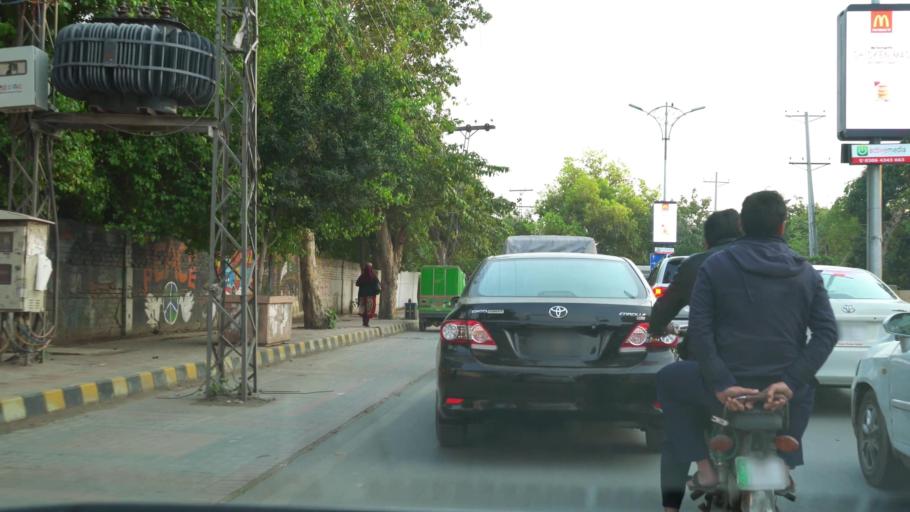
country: PK
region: Punjab
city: Lahore
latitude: 31.5083
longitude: 74.3503
